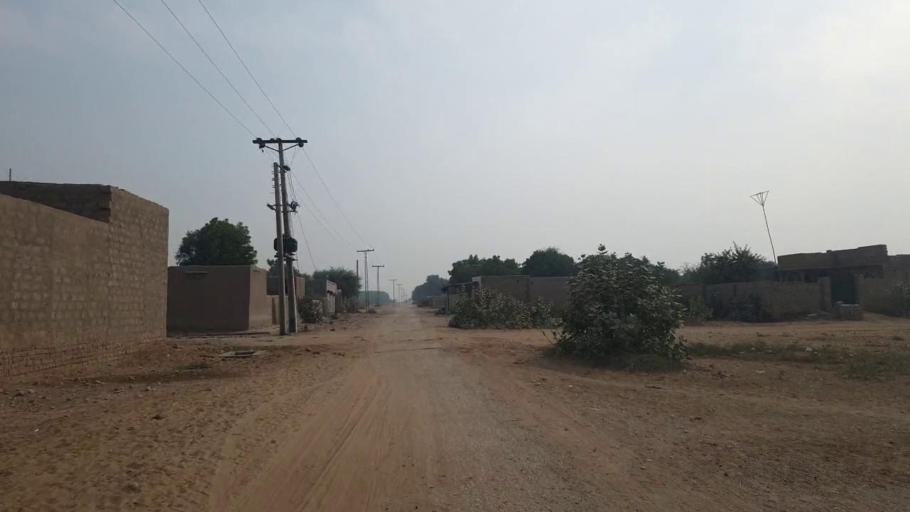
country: PK
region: Sindh
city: Sann
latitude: 26.0333
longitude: 68.1346
